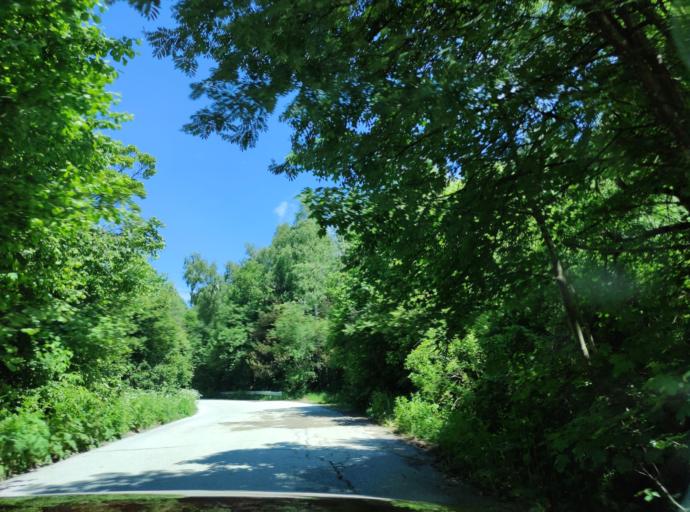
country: BG
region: Sofia-Capital
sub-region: Stolichna Obshtina
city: Sofia
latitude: 42.6331
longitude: 23.2318
